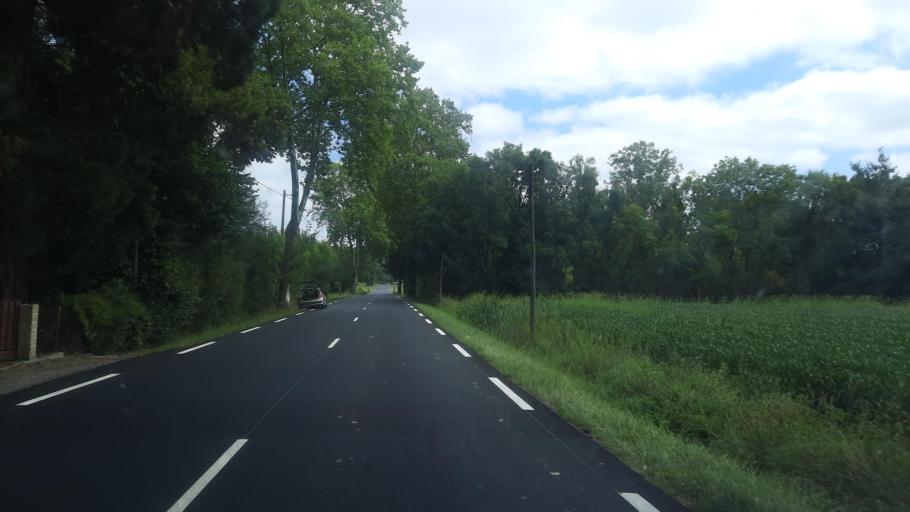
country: FR
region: Midi-Pyrenees
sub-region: Departement de la Haute-Garonne
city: Boulogne-sur-Gesse
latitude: 43.2884
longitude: 0.5359
